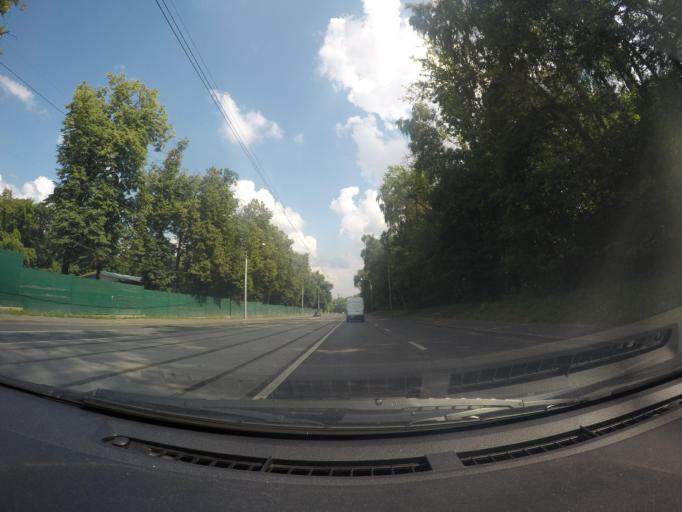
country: RU
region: Moscow
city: Rostokino
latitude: 55.8190
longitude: 37.6717
